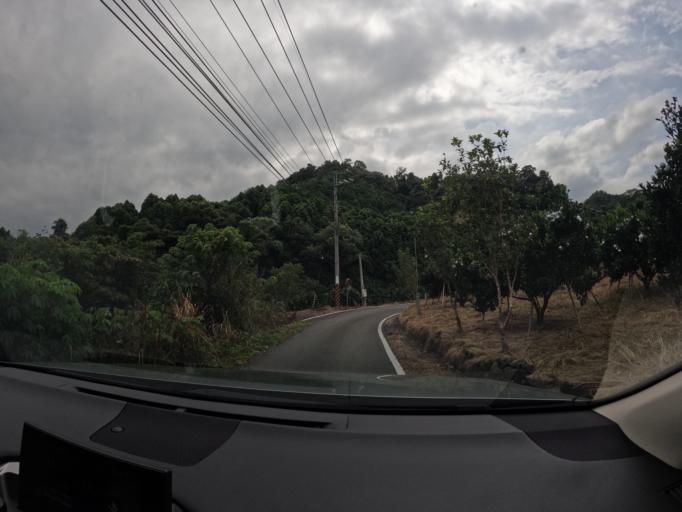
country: TW
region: Taiwan
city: Fengyuan
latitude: 24.3145
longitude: 120.8801
